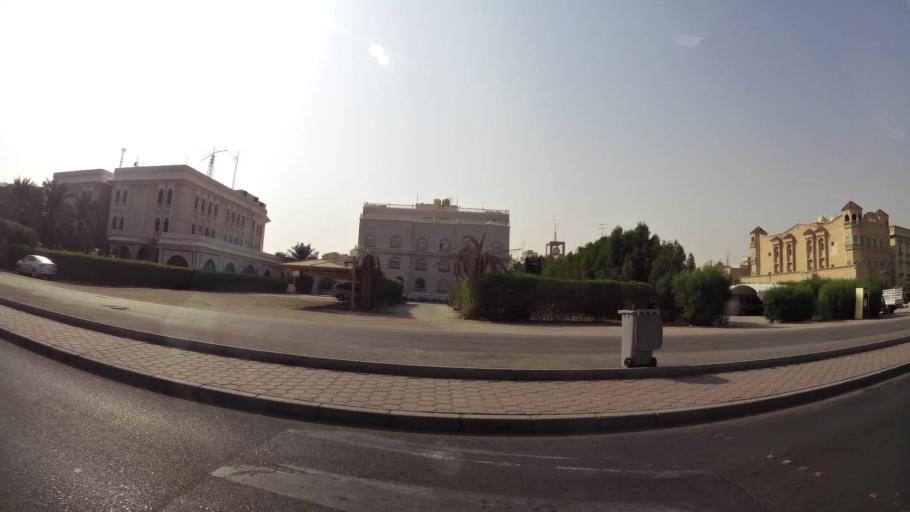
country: KW
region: Al Asimah
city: Ar Rabiyah
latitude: 29.2744
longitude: 47.8789
